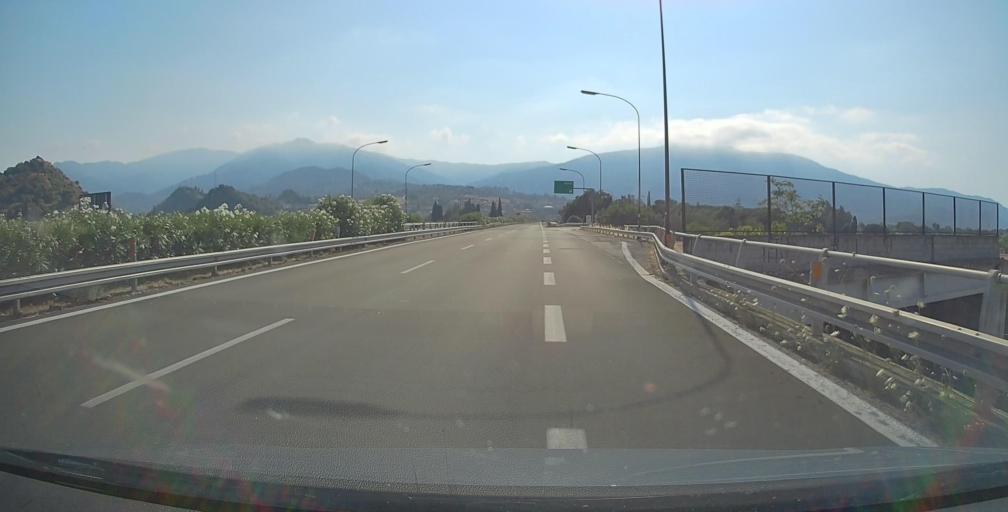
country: IT
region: Sicily
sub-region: Messina
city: Patti
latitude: 38.1439
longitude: 15.0028
